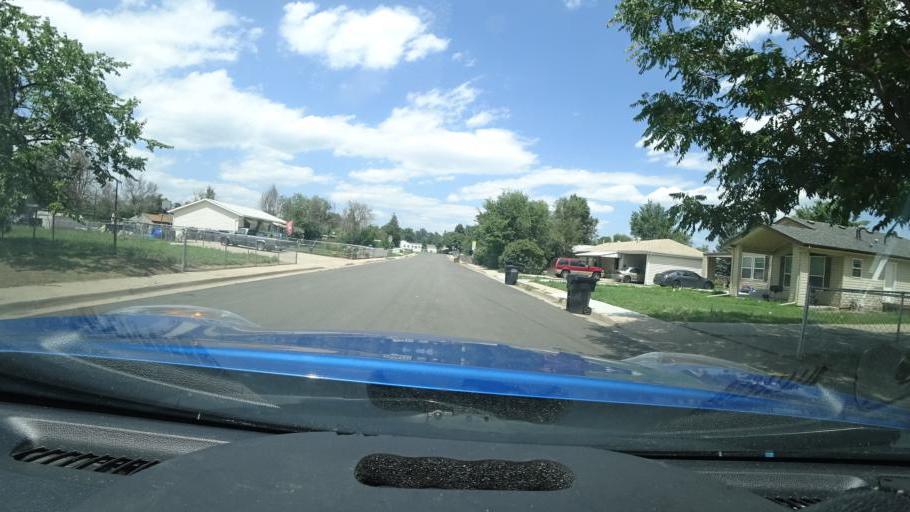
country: US
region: Colorado
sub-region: Arapahoe County
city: Sheridan
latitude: 39.6810
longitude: -105.0133
